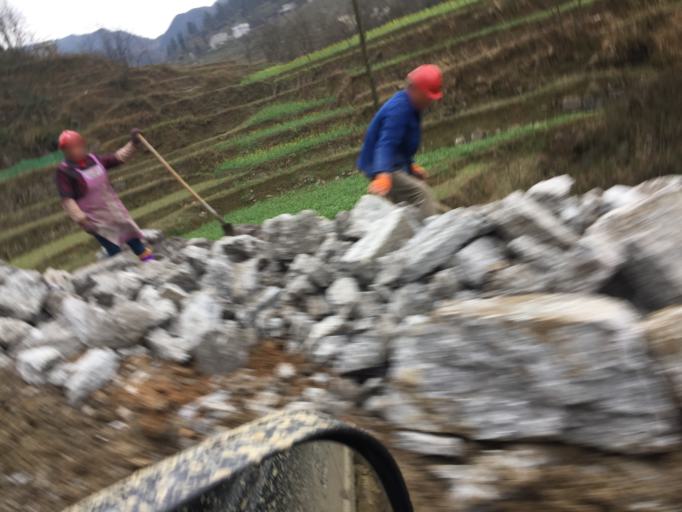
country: CN
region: Guizhou Sheng
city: Changfeng
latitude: 28.4902
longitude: 108.0612
